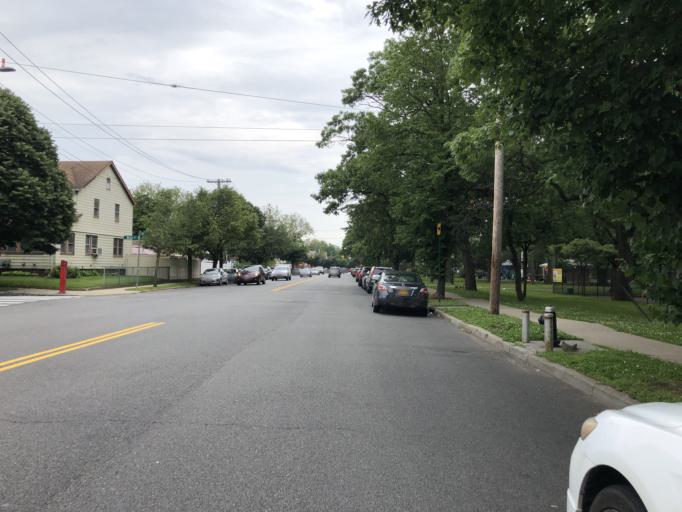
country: US
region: New York
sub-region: Nassau County
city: South Valley Stream
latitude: 40.6630
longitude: -73.7411
